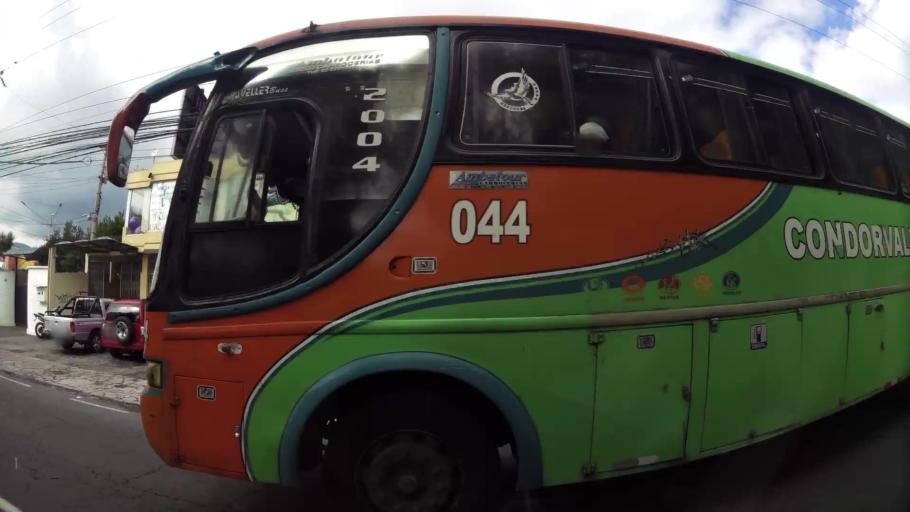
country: EC
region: Pichincha
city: Sangolqui
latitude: -0.3153
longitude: -78.4507
